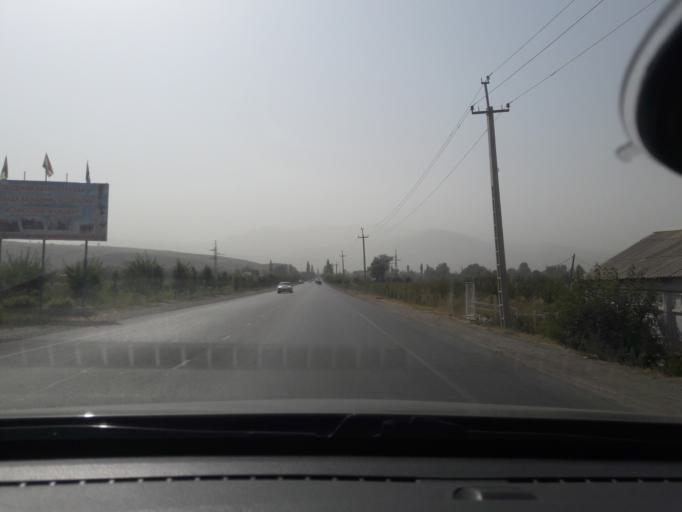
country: TJ
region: Republican Subordination
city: Vahdat
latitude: 38.5294
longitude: 69.0262
